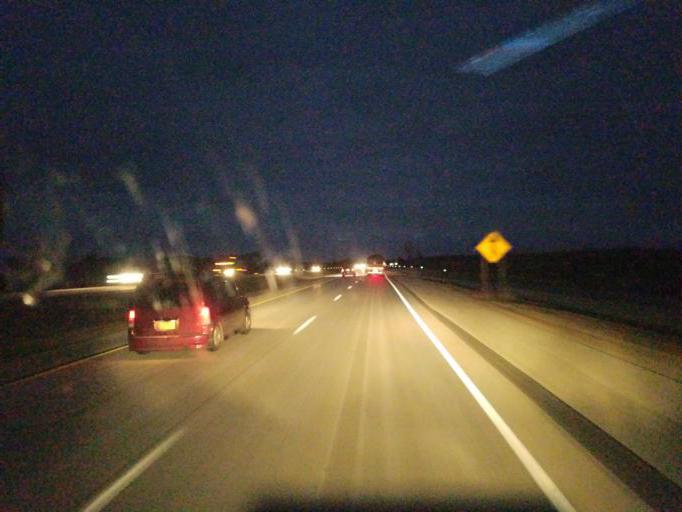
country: US
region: Iowa
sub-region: Guthrie County
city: Guthrie Center
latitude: 41.4967
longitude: -94.5597
